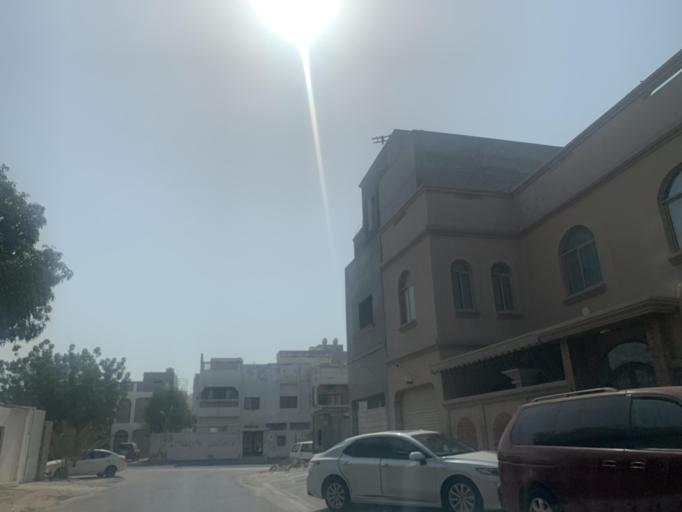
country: BH
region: Manama
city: Jidd Hafs
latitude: 26.2125
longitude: 50.4661
